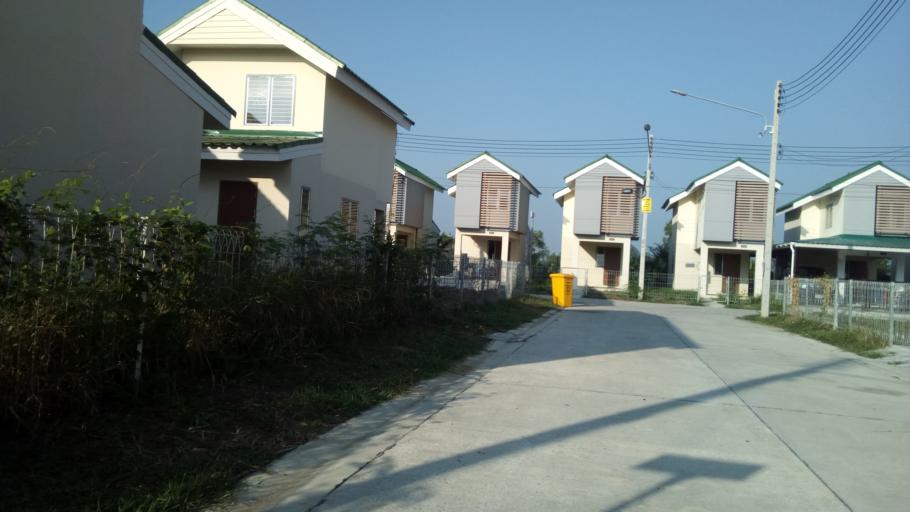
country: TH
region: Pathum Thani
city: Ban Rangsit
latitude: 14.0426
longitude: 100.8400
